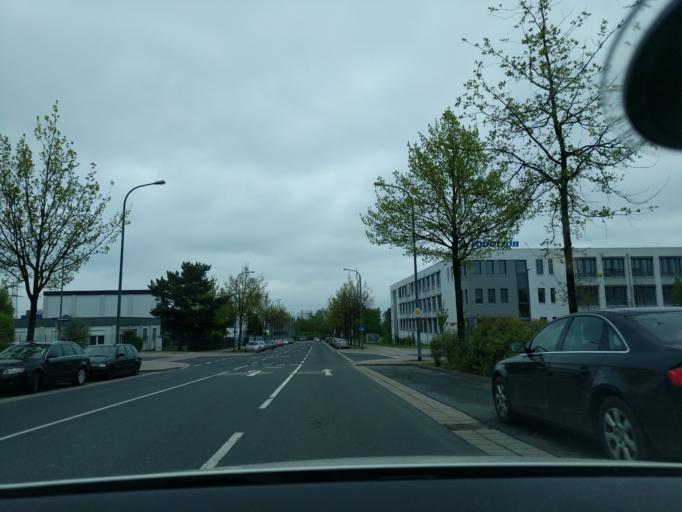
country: DE
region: Saxony
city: Bannewitz
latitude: 51.0097
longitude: 13.7010
